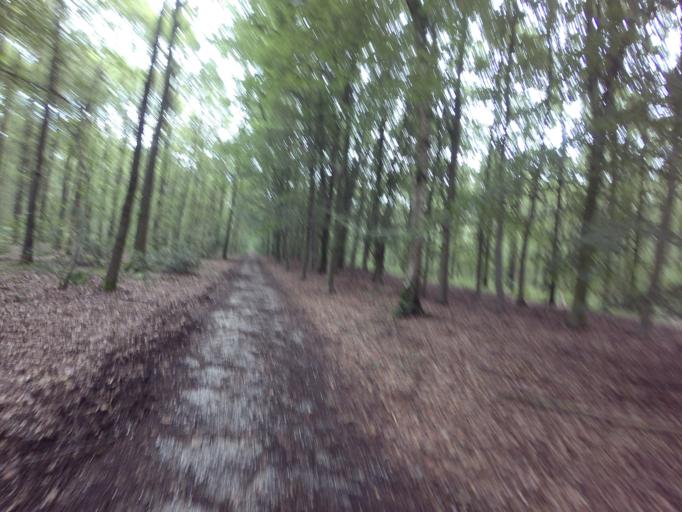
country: BE
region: Wallonia
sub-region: Province de Liege
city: Plombieres
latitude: 50.7627
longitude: 5.9756
